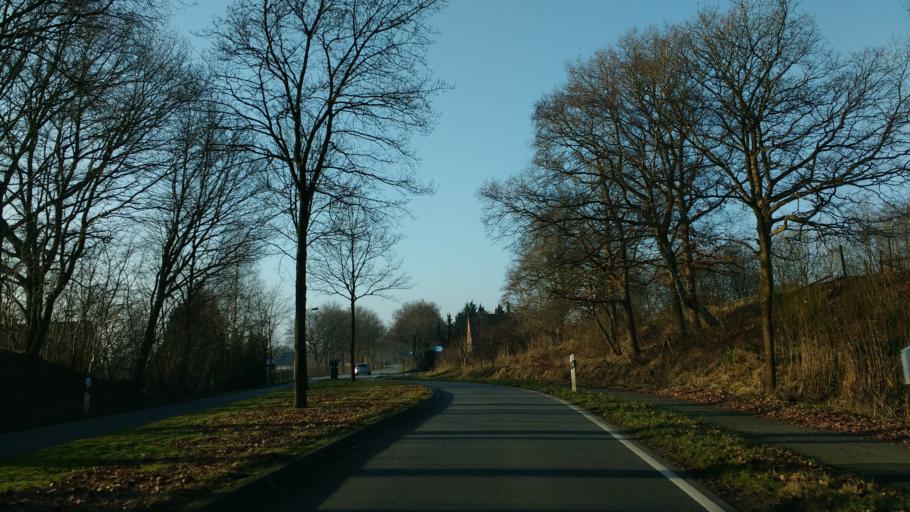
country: DE
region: Schleswig-Holstein
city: Wacken
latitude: 54.0217
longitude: 9.3894
